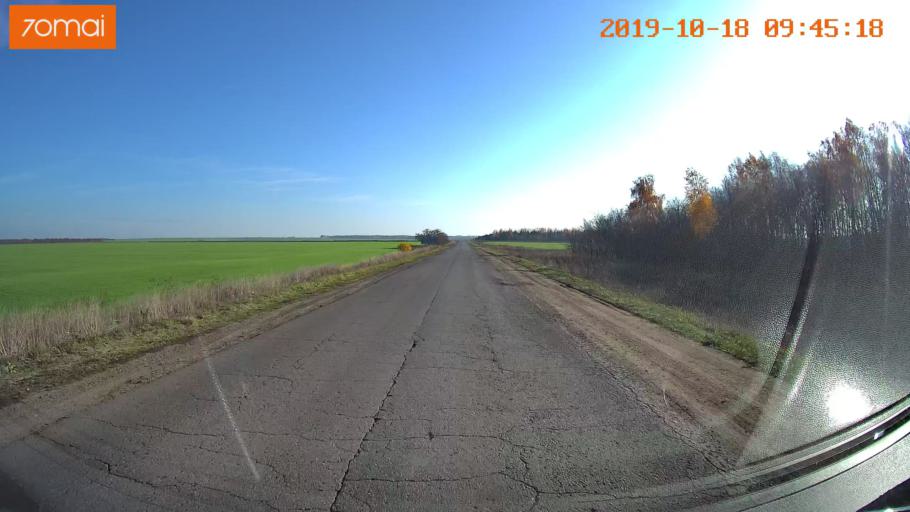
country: RU
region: Tula
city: Kazachka
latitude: 53.3124
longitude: 38.1865
